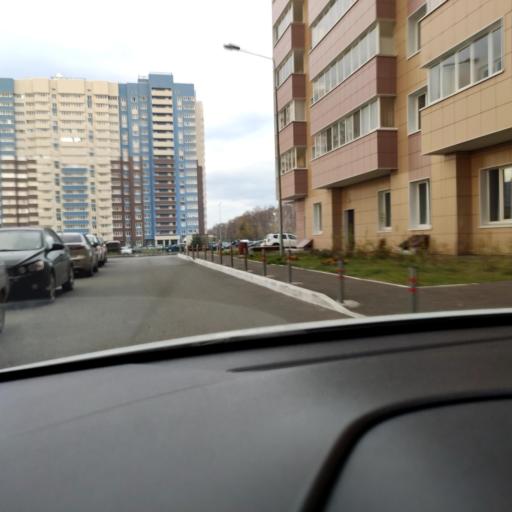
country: RU
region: Tatarstan
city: Osinovo
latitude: 55.8682
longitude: 48.8829
